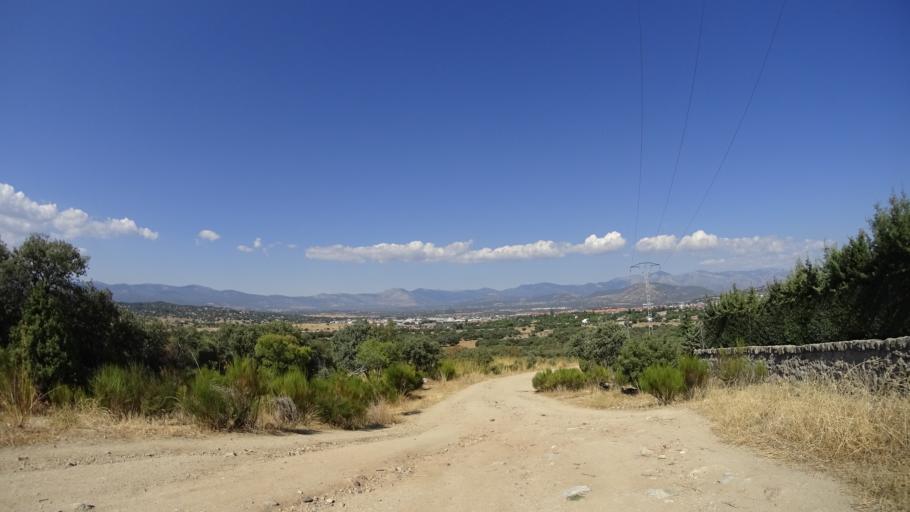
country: ES
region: Madrid
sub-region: Provincia de Madrid
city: Galapagar
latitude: 40.6065
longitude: -4.0115
